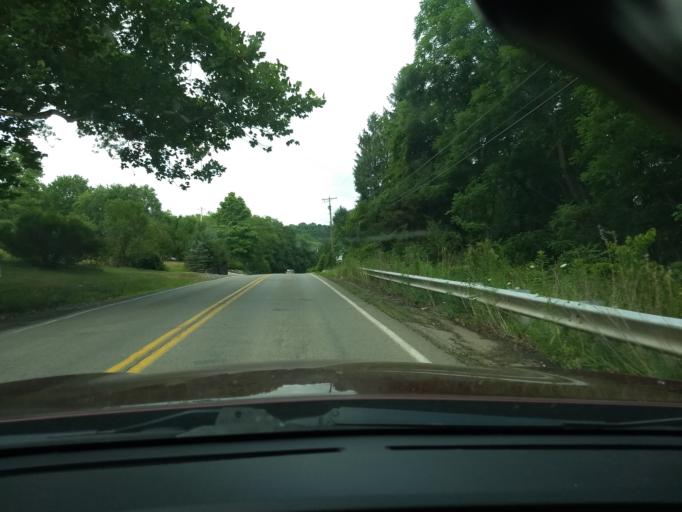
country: US
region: Pennsylvania
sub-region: Butler County
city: Cranberry Township
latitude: 40.6423
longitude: -80.1344
